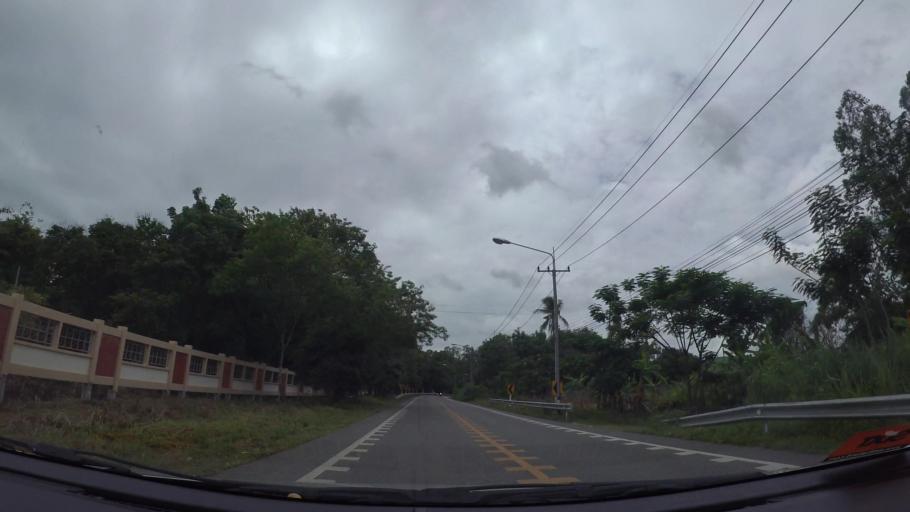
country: TH
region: Chon Buri
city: Si Racha
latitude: 13.1891
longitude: 100.9643
